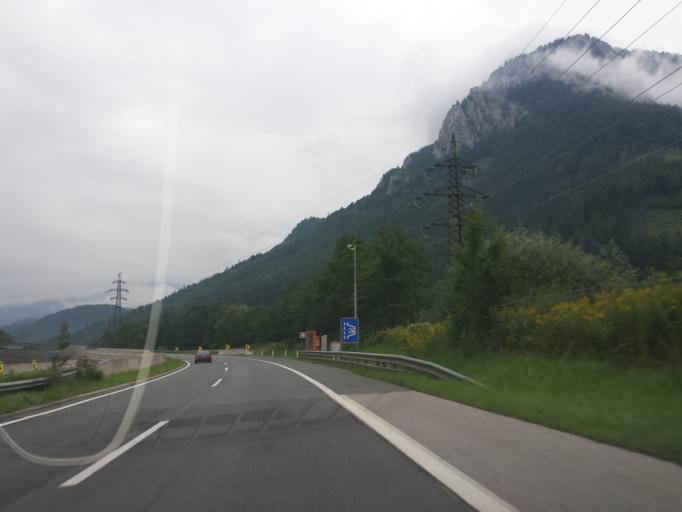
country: AT
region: Styria
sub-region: Politischer Bezirk Graz-Umgebung
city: Rothelstein
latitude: 47.3128
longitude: 15.3733
